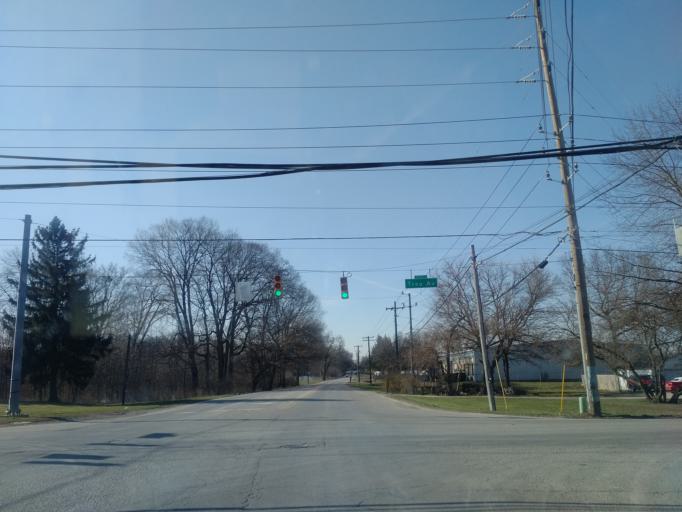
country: US
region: Indiana
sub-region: Marion County
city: Indianapolis
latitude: 39.7225
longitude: -86.1682
